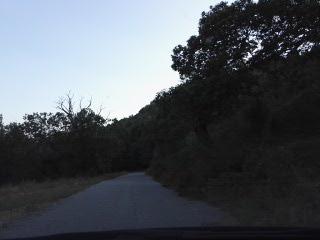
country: IT
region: Calabria
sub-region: Provincia di Vibo-Valentia
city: Nardodipace
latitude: 38.4218
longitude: 16.3500
